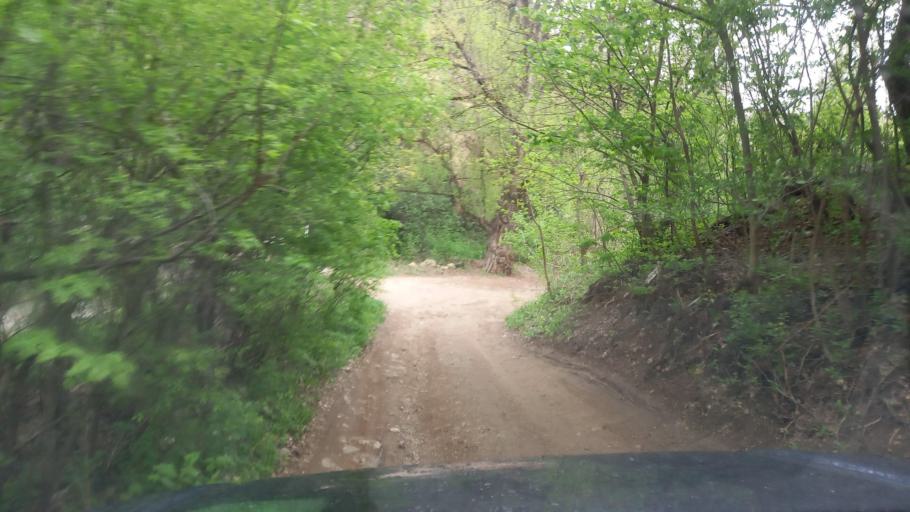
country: RU
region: Stavropol'skiy
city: Kislovodsk
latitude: 43.8915
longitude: 42.7079
